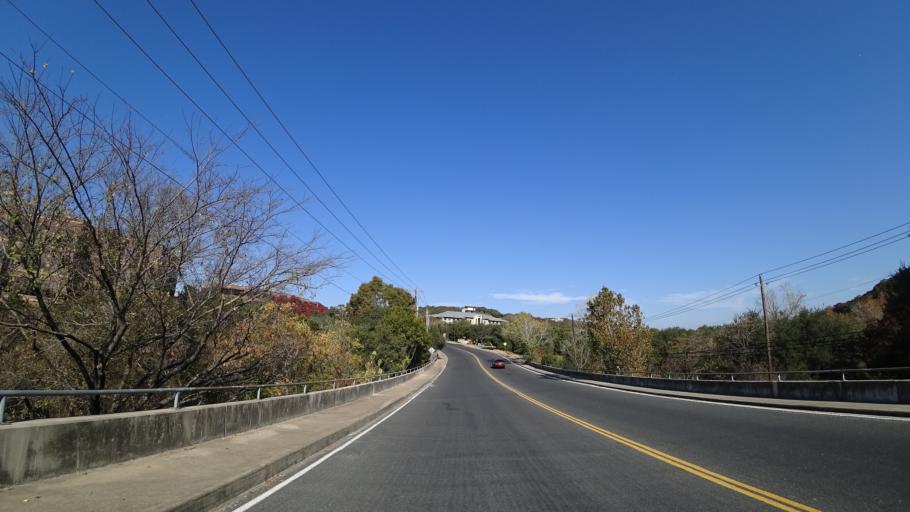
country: US
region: Texas
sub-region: Williamson County
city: Jollyville
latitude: 30.3860
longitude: -97.7671
